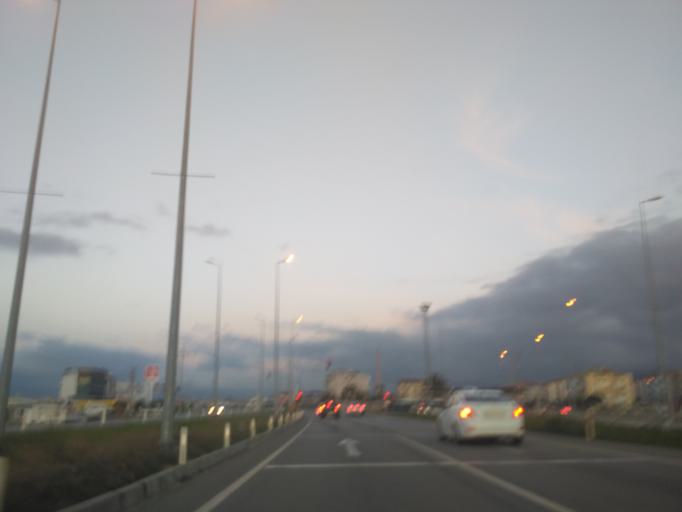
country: TR
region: Balikesir
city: Burhaniye
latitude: 39.4889
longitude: 26.9583
